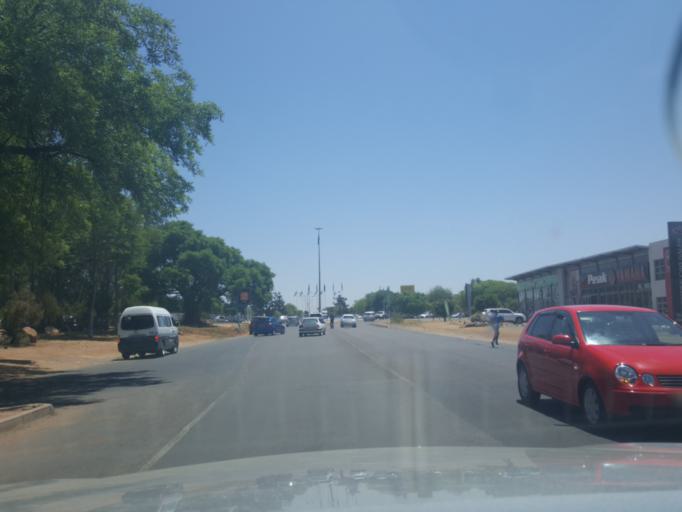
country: BW
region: South East
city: Gaborone
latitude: -24.6883
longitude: 25.8849
